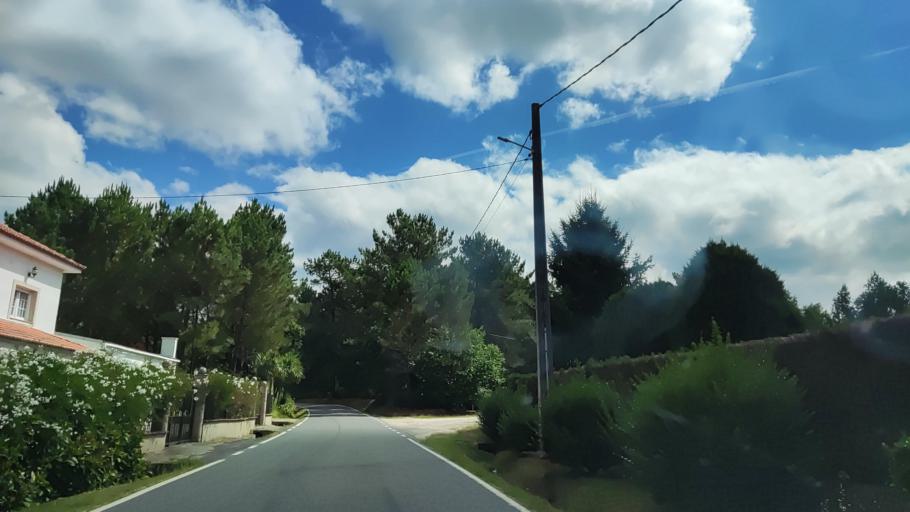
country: ES
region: Galicia
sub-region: Provincia da Coruna
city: Padron
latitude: 42.7820
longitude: -8.6640
